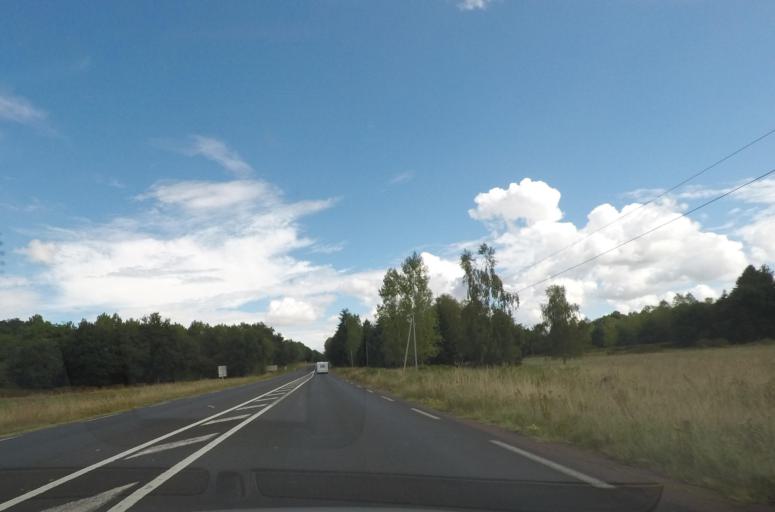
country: FR
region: Pays de la Loire
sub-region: Departement de la Sarthe
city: Parigne-le-Polin
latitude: 47.8462
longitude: 0.0908
